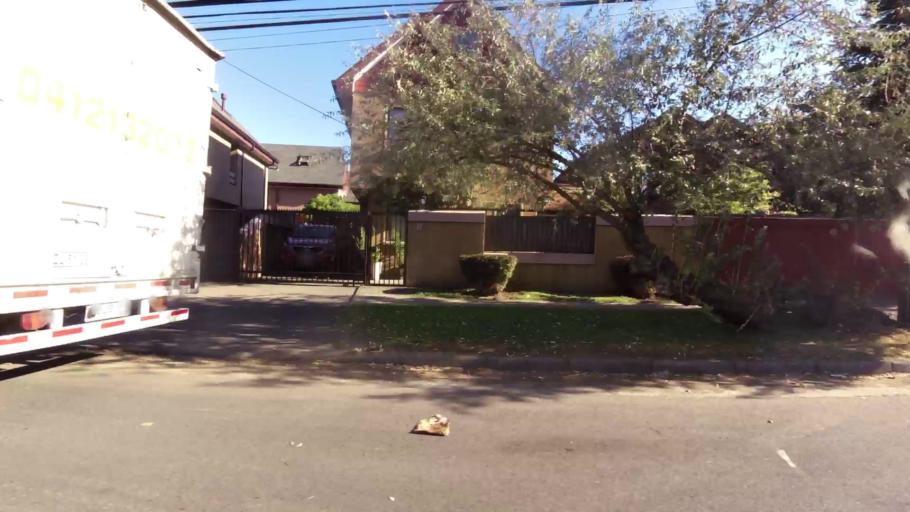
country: CL
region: Biobio
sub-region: Provincia de Concepcion
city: Concepcion
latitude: -36.8345
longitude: -73.1076
